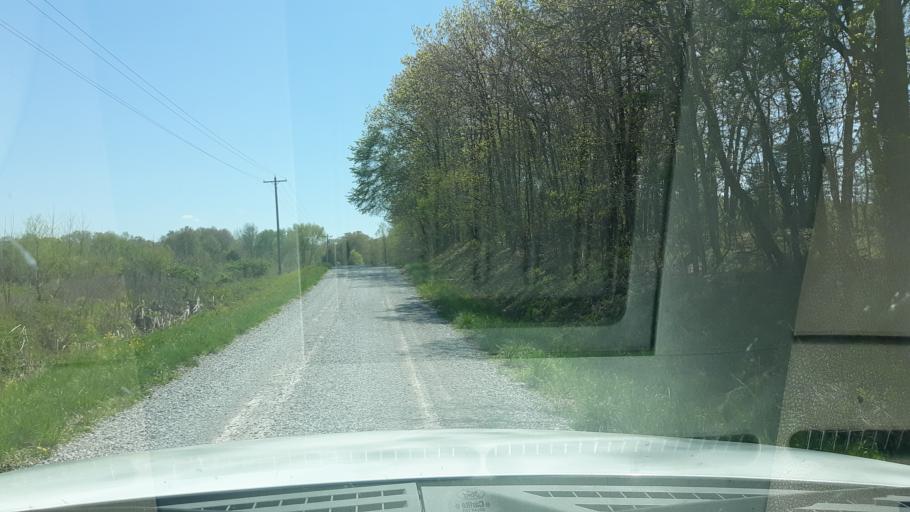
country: US
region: Illinois
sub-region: Saline County
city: Harrisburg
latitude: 37.8718
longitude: -88.6422
